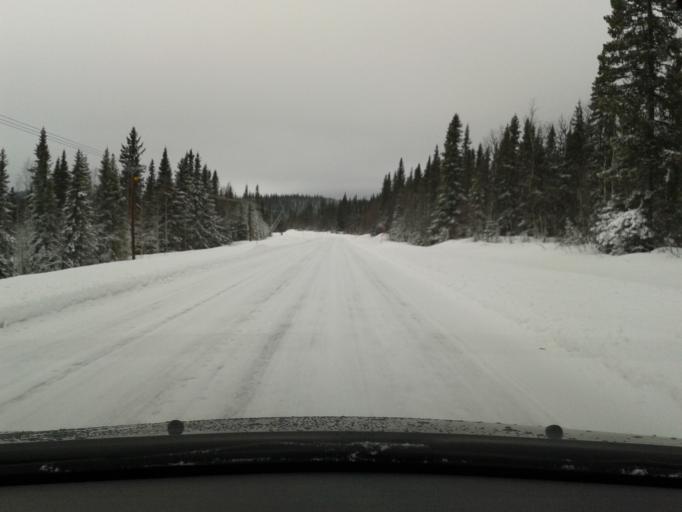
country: SE
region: Vaesterbotten
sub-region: Vilhelmina Kommun
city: Sjoberg
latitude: 65.1940
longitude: 15.9642
